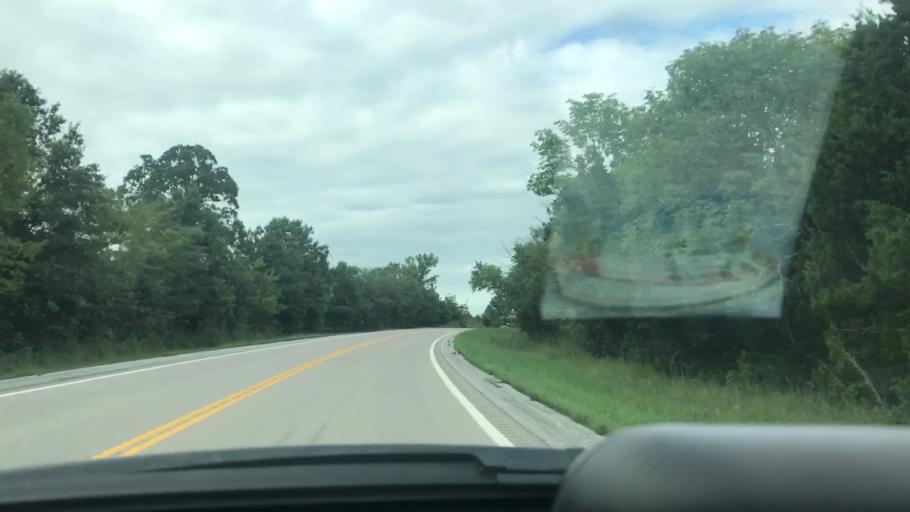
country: US
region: Missouri
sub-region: Benton County
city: Warsaw
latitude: 38.1256
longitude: -93.2802
